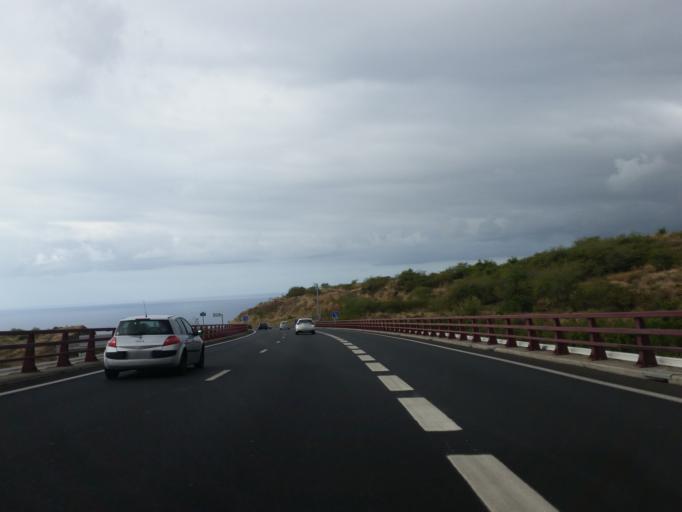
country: RE
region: Reunion
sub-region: Reunion
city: Saint-Paul
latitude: -21.0277
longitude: 55.2557
